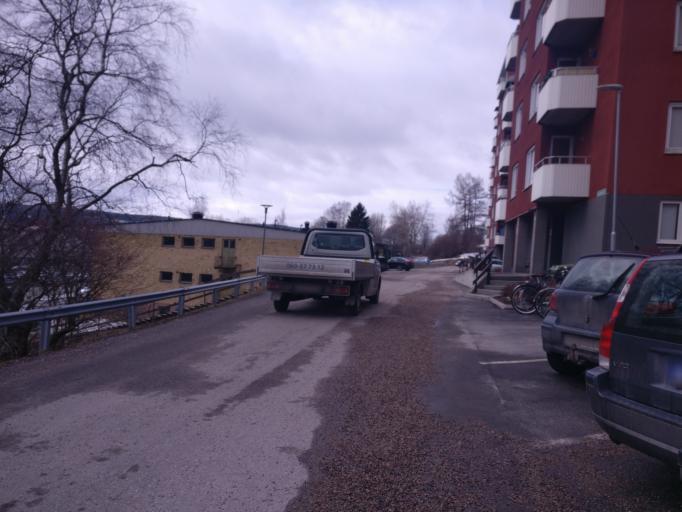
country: SE
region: Vaesternorrland
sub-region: Sundsvalls Kommun
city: Sundsvall
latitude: 62.3953
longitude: 17.2947
